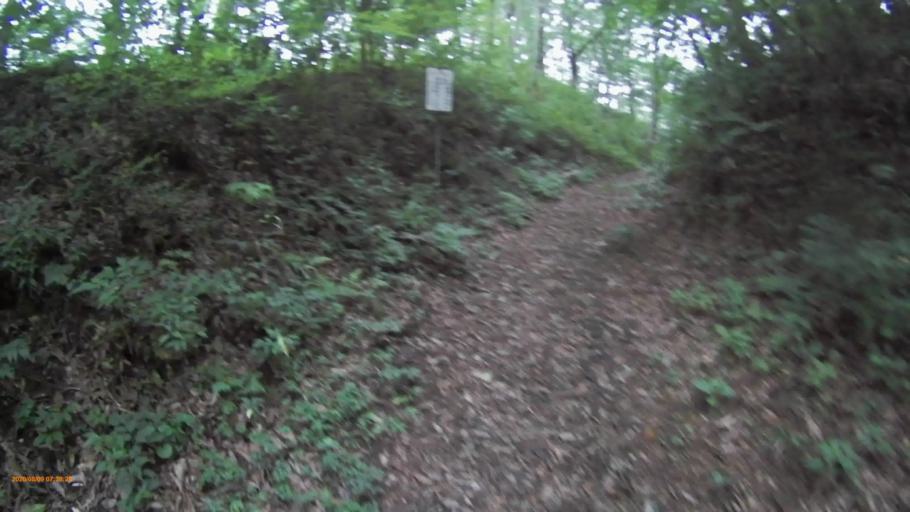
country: JP
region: Nagano
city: Tatsuno
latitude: 35.9585
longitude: 137.8048
